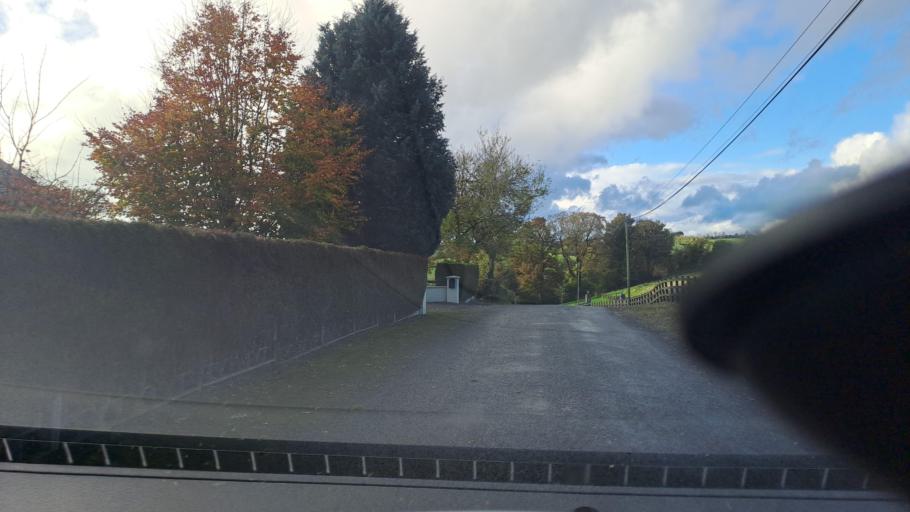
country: IE
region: Ulster
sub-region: An Cabhan
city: Bailieborough
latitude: 53.9383
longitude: -6.9590
